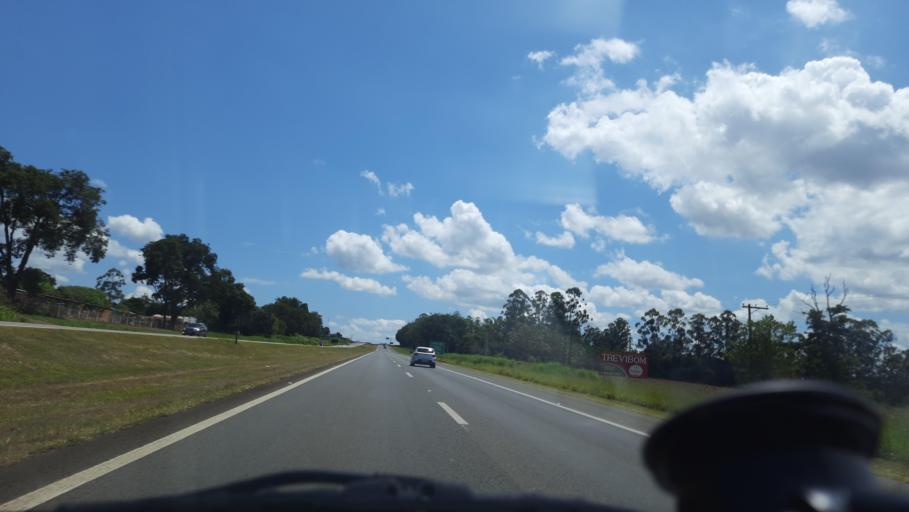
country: BR
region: Sao Paulo
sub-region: Moji-Guacu
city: Mogi-Gaucu
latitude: -22.2325
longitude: -46.9785
